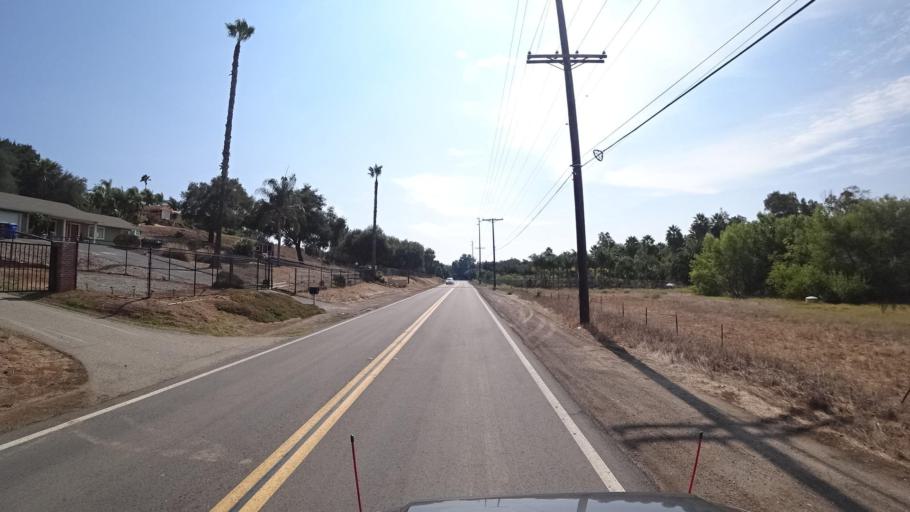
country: US
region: California
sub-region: San Diego County
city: Escondido
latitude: 33.1115
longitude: -117.0469
